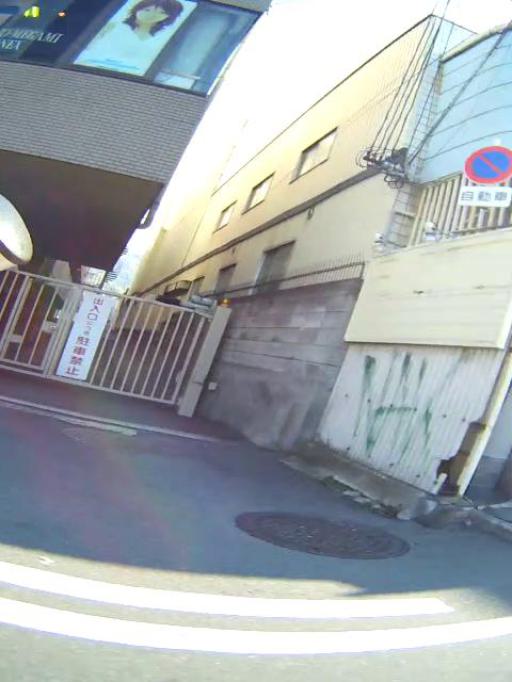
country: JP
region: Osaka
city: Daitocho
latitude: 34.6605
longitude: 135.6401
